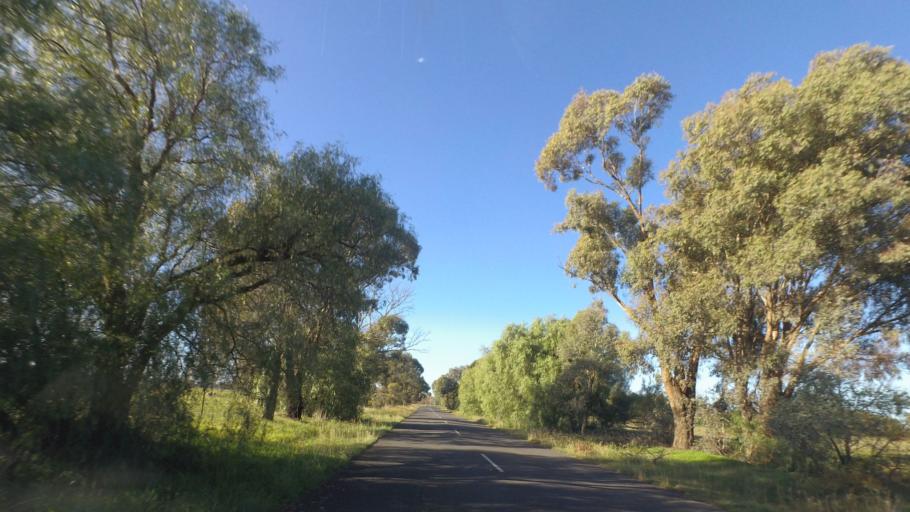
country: AU
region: Victoria
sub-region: Greater Bendigo
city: Epsom
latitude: -36.6477
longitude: 144.5297
